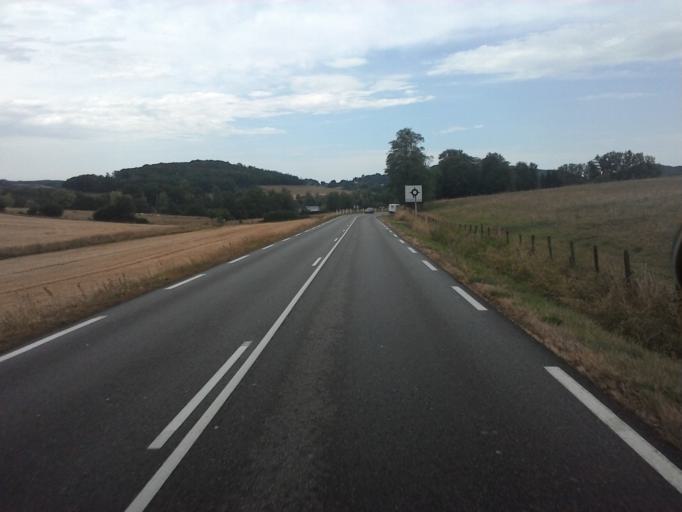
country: FR
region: Franche-Comte
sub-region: Departement du Jura
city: Poligny
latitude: 46.8187
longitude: 5.5933
